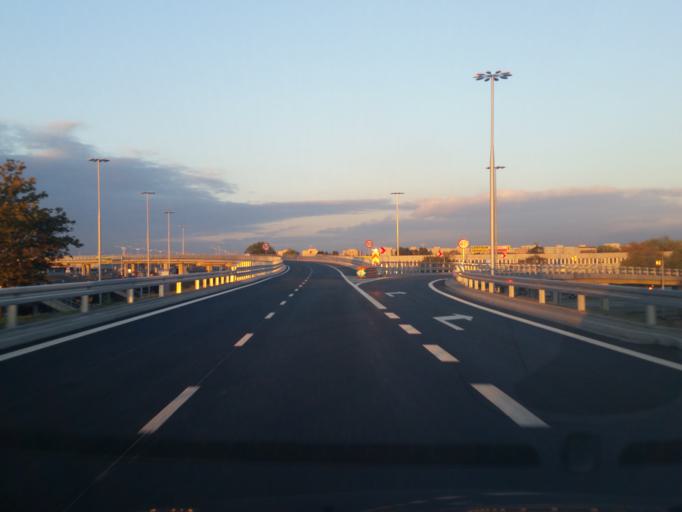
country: PL
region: Masovian Voivodeship
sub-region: Warszawa
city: Zoliborz
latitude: 52.2894
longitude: 21.0014
